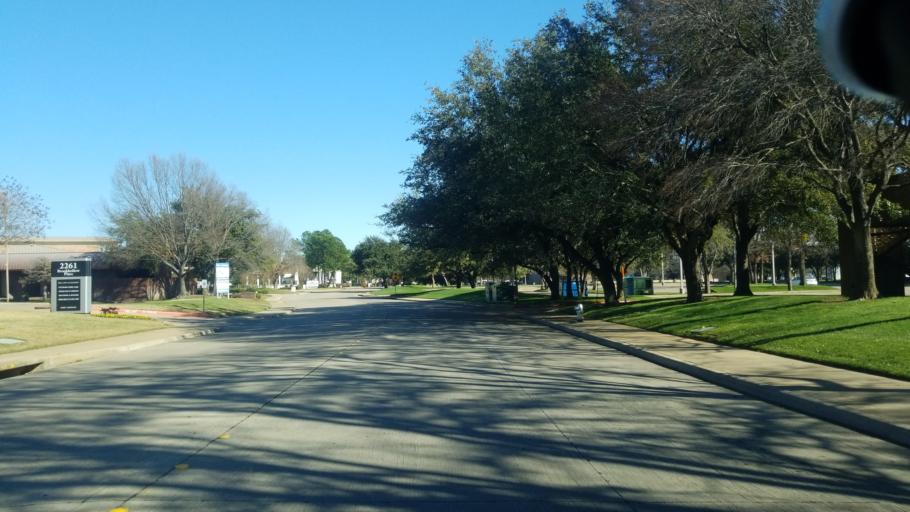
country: US
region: Texas
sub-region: Tarrant County
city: Arlington
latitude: 32.7633
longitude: -97.0701
